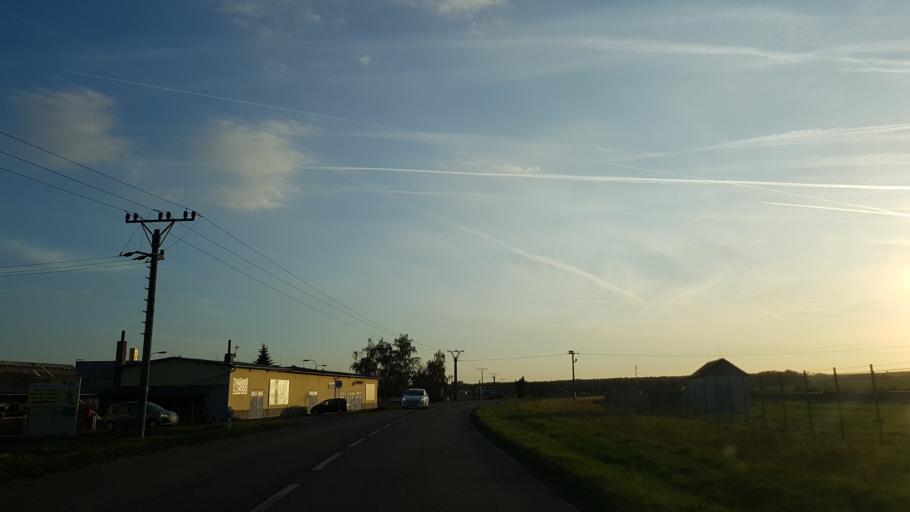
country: CZ
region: Zlin
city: Polesovice
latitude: 49.0210
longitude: 17.3524
